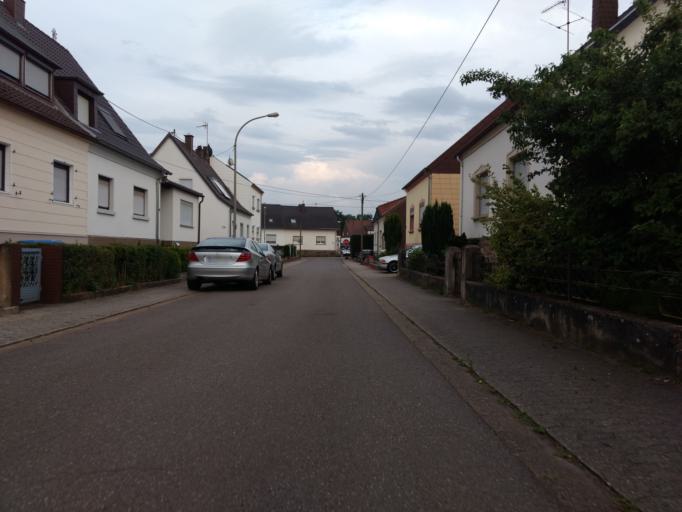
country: DE
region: Saarland
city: Wallerfangen
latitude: 49.3263
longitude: 6.7134
